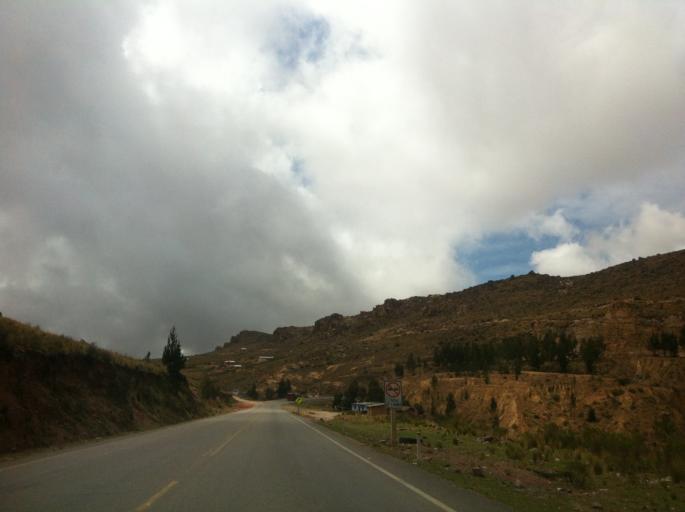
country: BO
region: Cochabamba
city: Irpa Irpa
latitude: -17.7000
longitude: -66.4788
